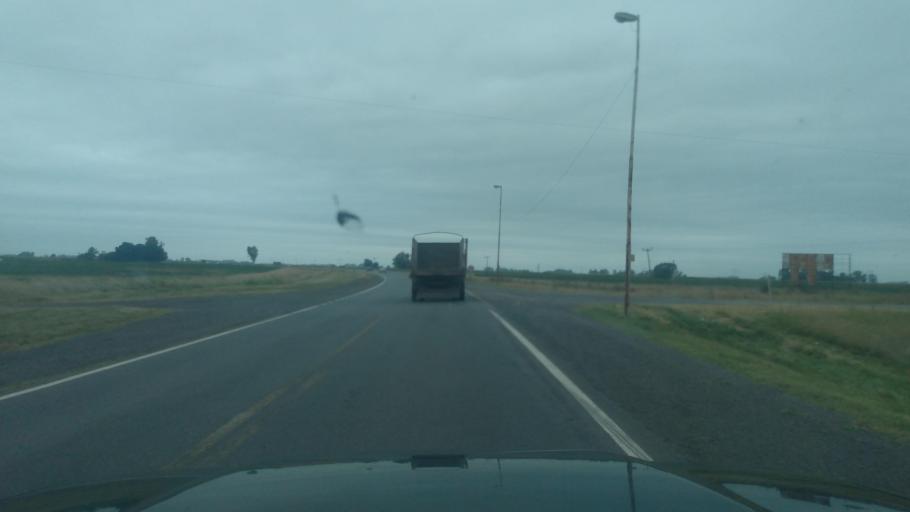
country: AR
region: Buenos Aires
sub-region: Partido de Nueve de Julio
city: Nueve de Julio
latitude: -35.3970
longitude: -60.7462
